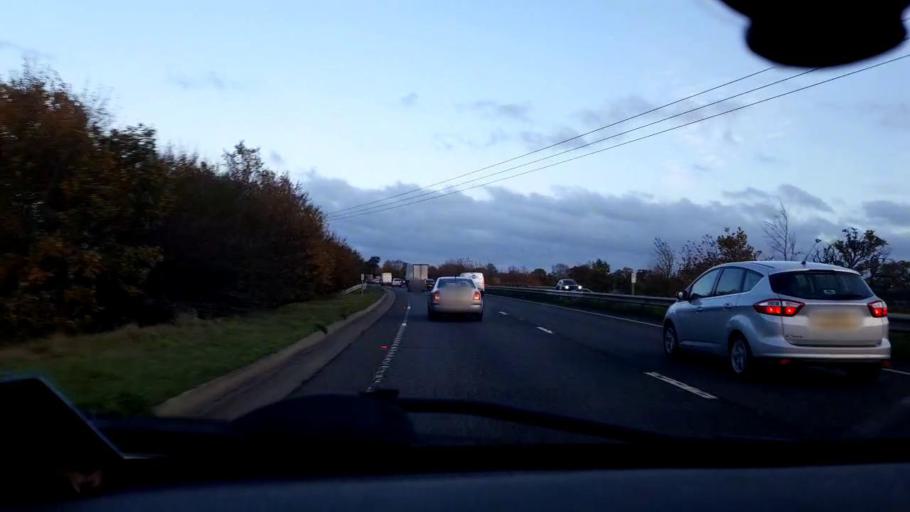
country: GB
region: England
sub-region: Norfolk
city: Cringleford
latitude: 52.5861
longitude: 1.2582
